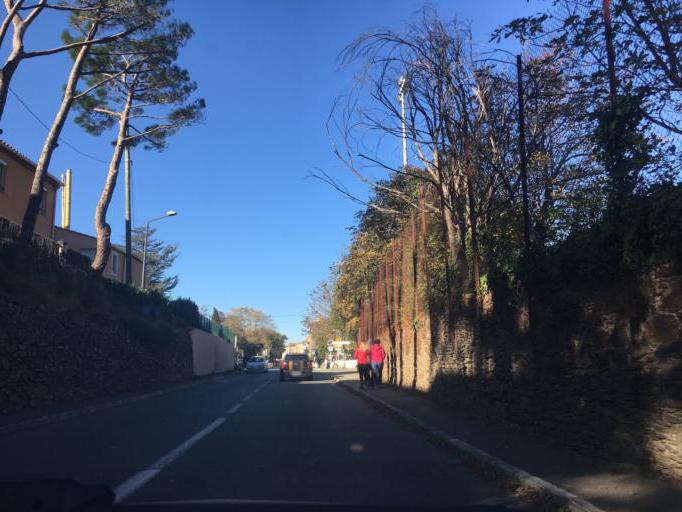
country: FR
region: Provence-Alpes-Cote d'Azur
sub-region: Departement du Var
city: La Garde-Freinet
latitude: 43.3138
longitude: 6.4713
